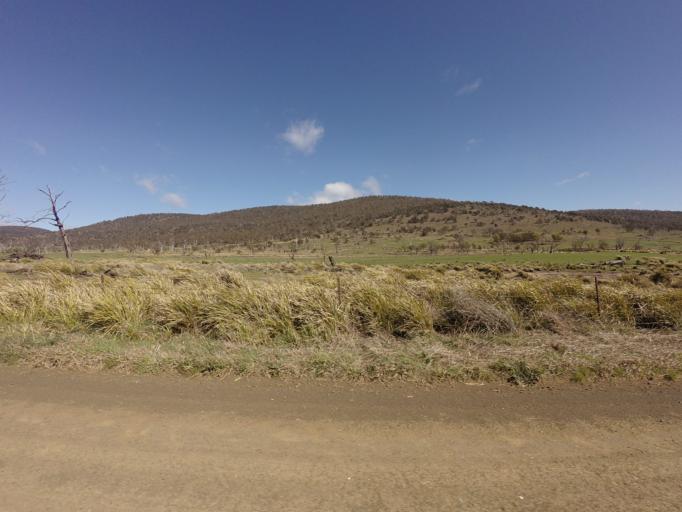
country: AU
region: Tasmania
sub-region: Northern Midlands
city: Evandale
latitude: -41.9320
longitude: 147.4166
